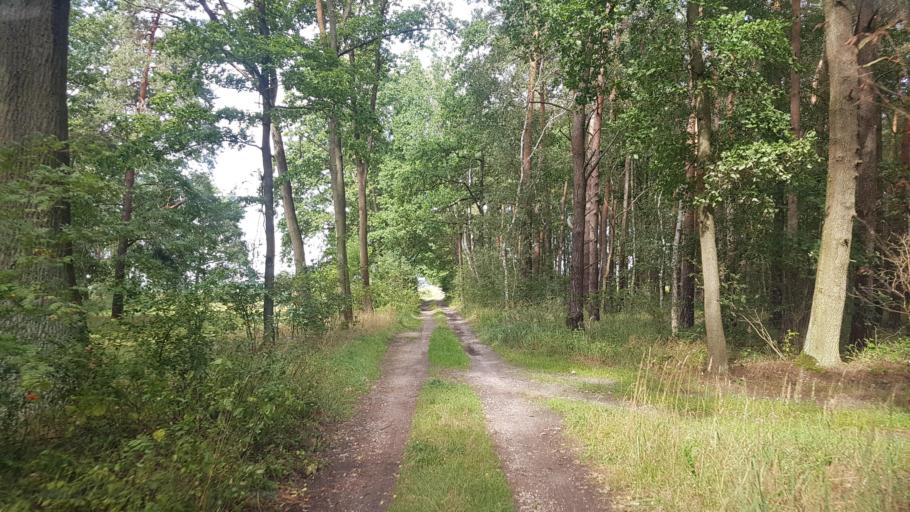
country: DE
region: Brandenburg
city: Bronkow
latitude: 51.6339
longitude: 13.8826
